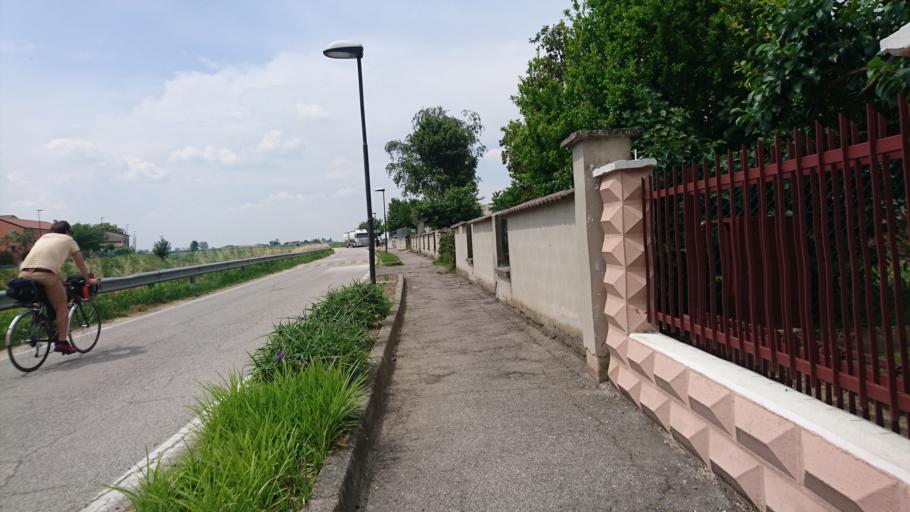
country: IT
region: Veneto
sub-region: Provincia di Rovigo
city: Giacciano con Baruchella
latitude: 45.0685
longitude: 11.4502
